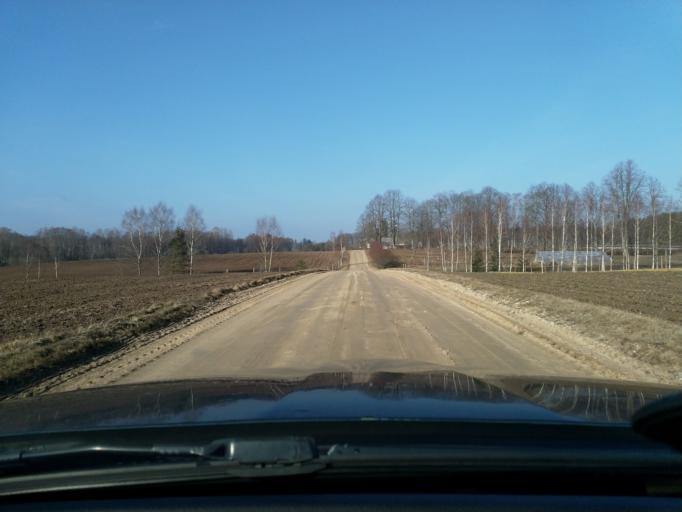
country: LV
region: Kuldigas Rajons
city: Kuldiga
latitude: 56.8704
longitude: 21.9456
